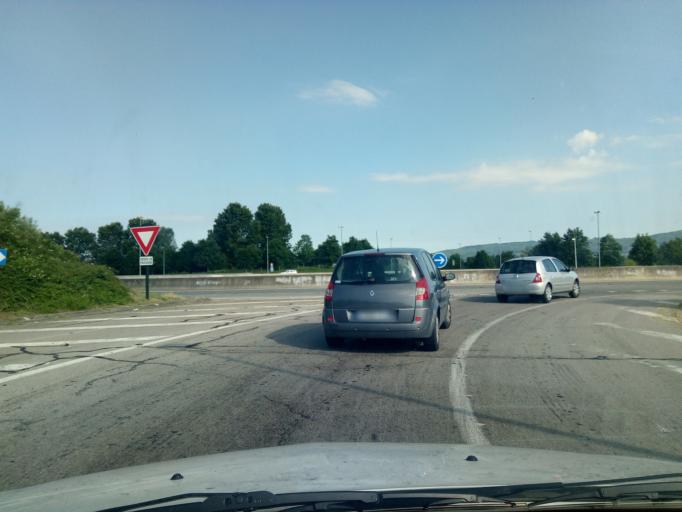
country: FR
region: Rhone-Alpes
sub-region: Departement de l'Isere
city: Izeaux
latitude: 45.3645
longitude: 5.4212
